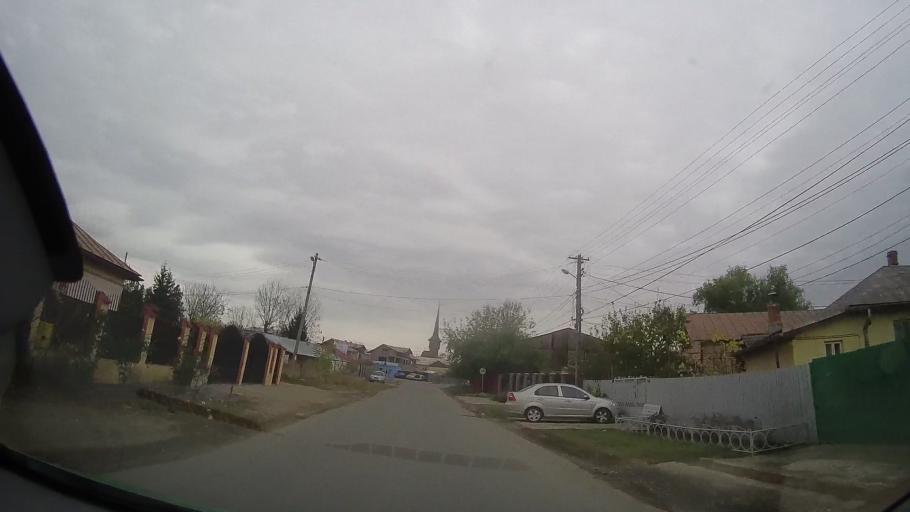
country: RO
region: Prahova
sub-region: Oras Mizil
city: Mizil
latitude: 45.0009
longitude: 26.4331
